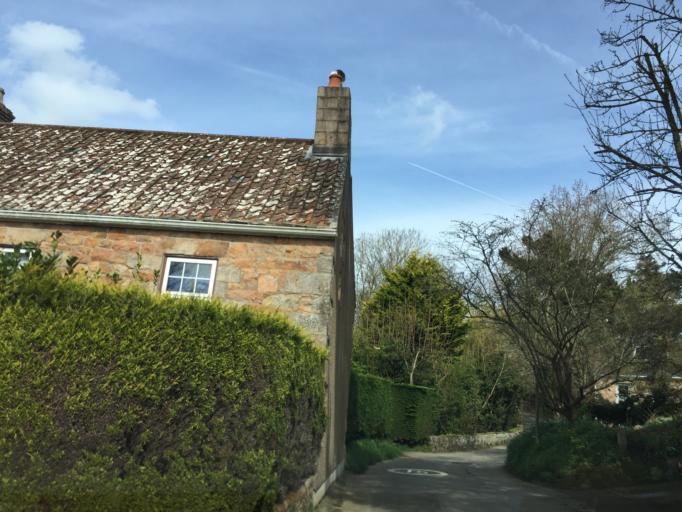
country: JE
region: St Helier
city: Saint Helier
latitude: 49.2391
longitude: -2.1808
